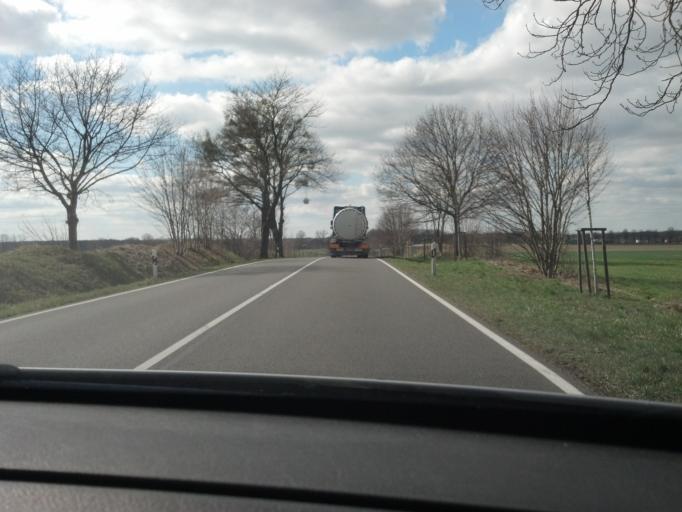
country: DE
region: Mecklenburg-Vorpommern
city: Rechlin
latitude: 53.3156
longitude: 12.7366
